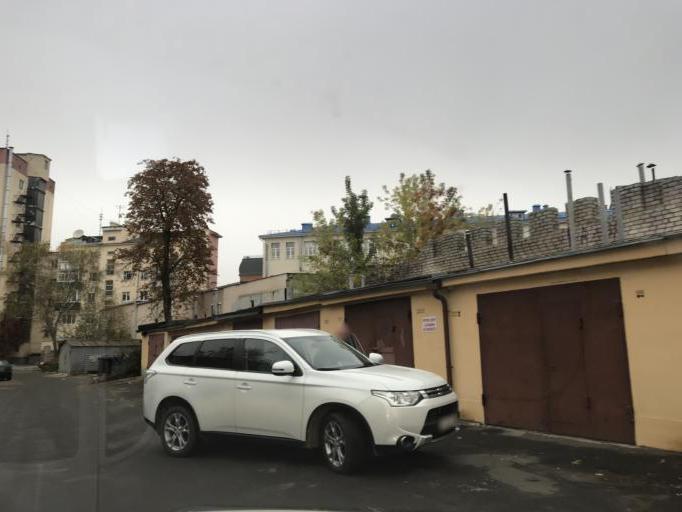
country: BY
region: Mogilev
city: Mahilyow
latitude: 53.8962
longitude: 30.3327
